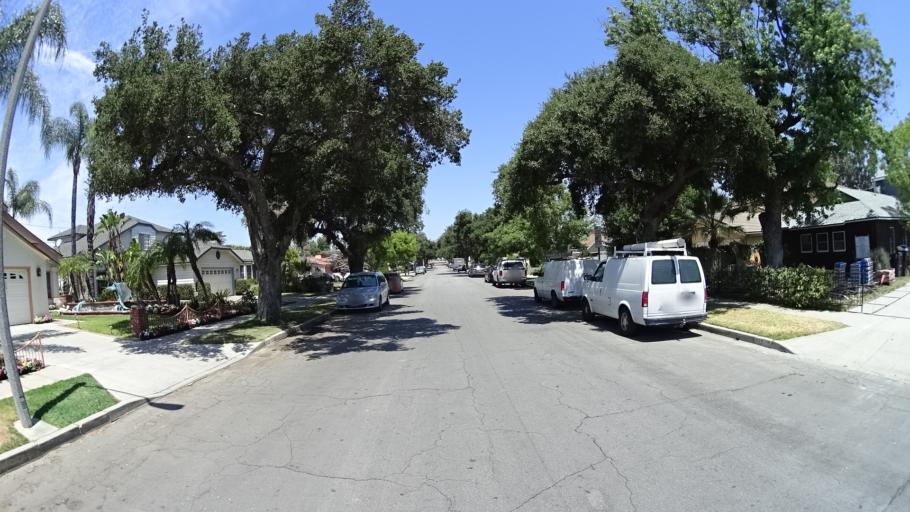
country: US
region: California
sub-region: Los Angeles County
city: Burbank
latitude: 34.1739
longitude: -118.3321
